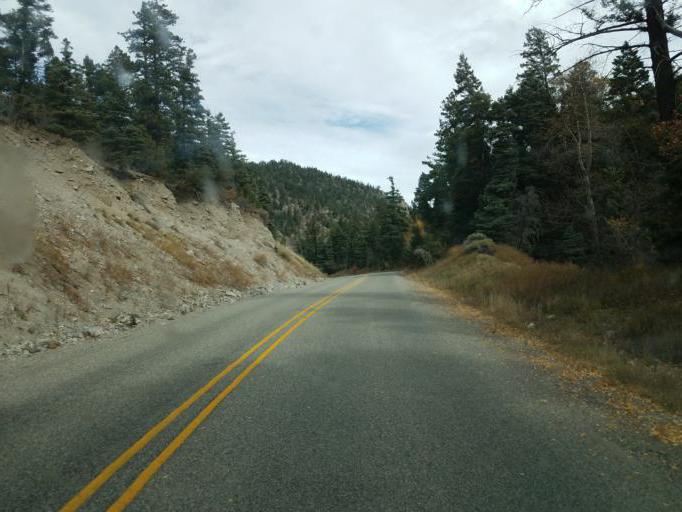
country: US
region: New Mexico
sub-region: Taos County
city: Arroyo Seco
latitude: 36.5563
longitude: -105.5375
